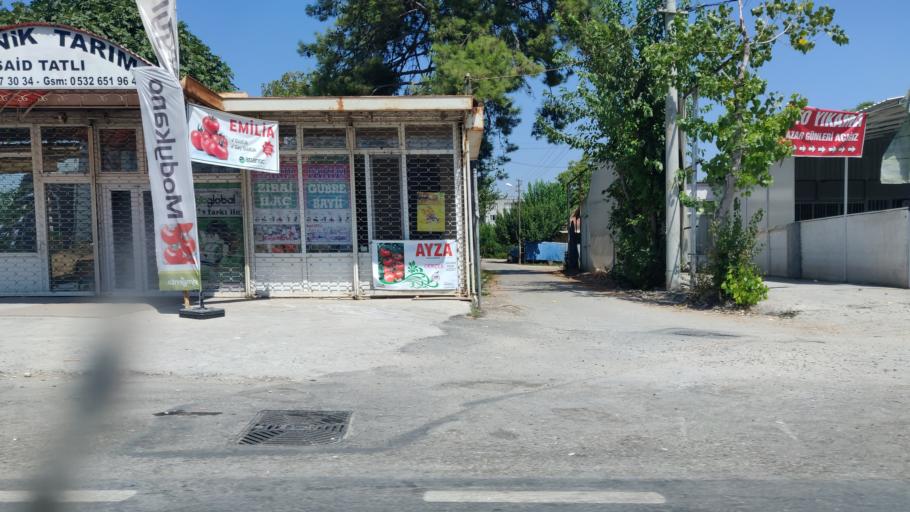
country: TR
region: Antalya
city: Antalya
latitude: 36.9000
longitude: 30.6300
